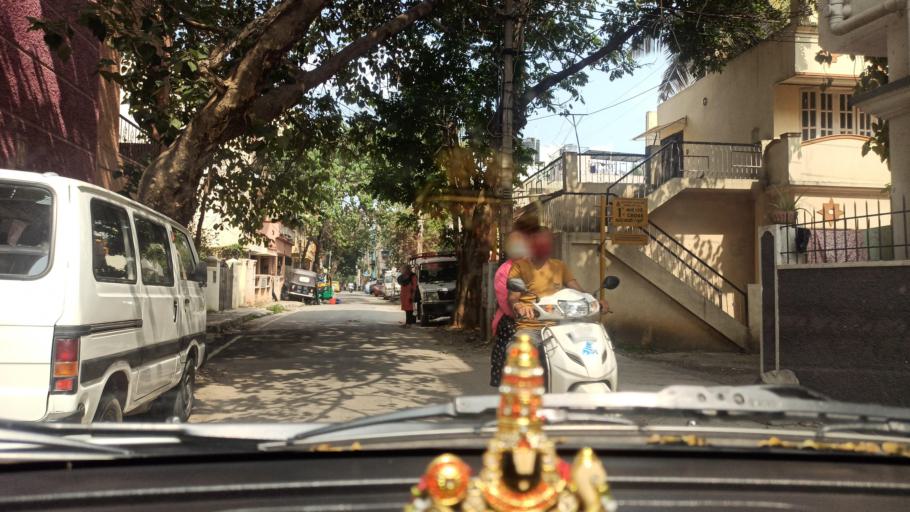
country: IN
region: Karnataka
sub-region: Bangalore Urban
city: Bangalore
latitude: 13.0125
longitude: 77.6700
